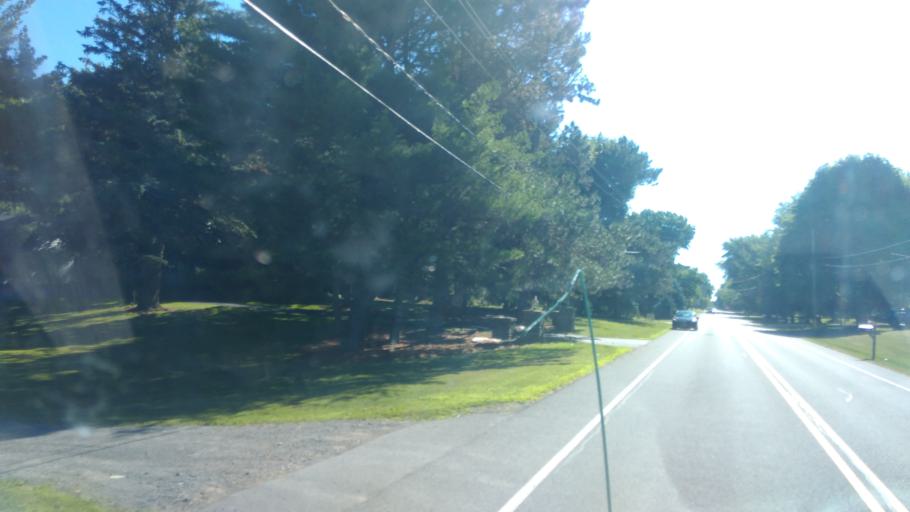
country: US
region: New York
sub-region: Monroe County
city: Webster
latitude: 43.2373
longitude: -77.4647
